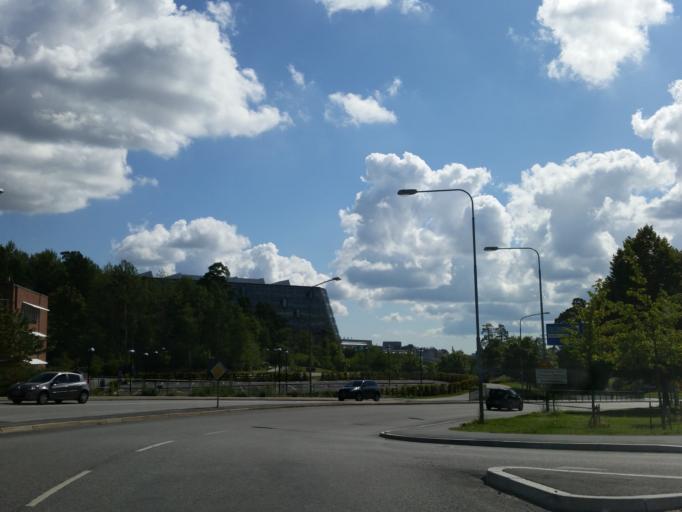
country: SE
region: Stockholm
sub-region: Solna Kommun
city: Solna
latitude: 59.3508
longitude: 18.0048
